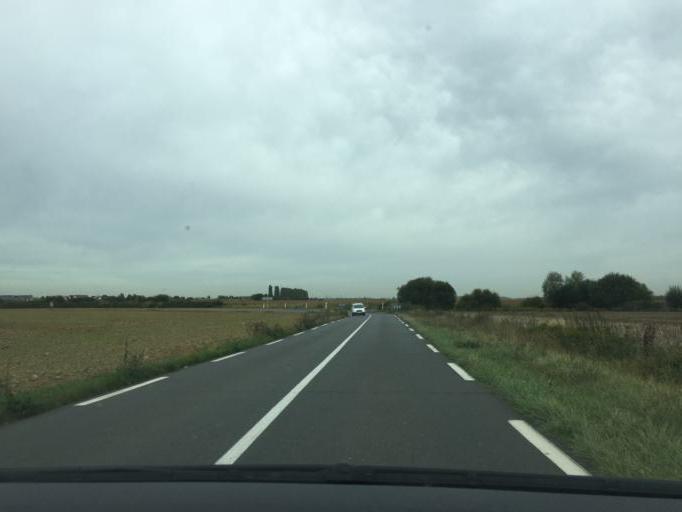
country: FR
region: Ile-de-France
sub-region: Departement de l'Essonne
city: Villiers-le-Bacle
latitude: 48.7391
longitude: 2.1258
